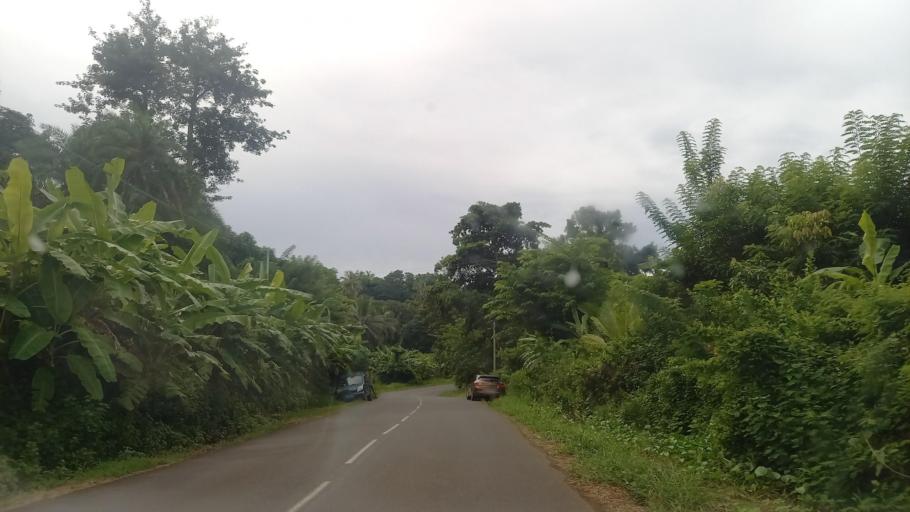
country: YT
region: Boueni
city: Boueni
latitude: -12.9145
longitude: 45.1015
